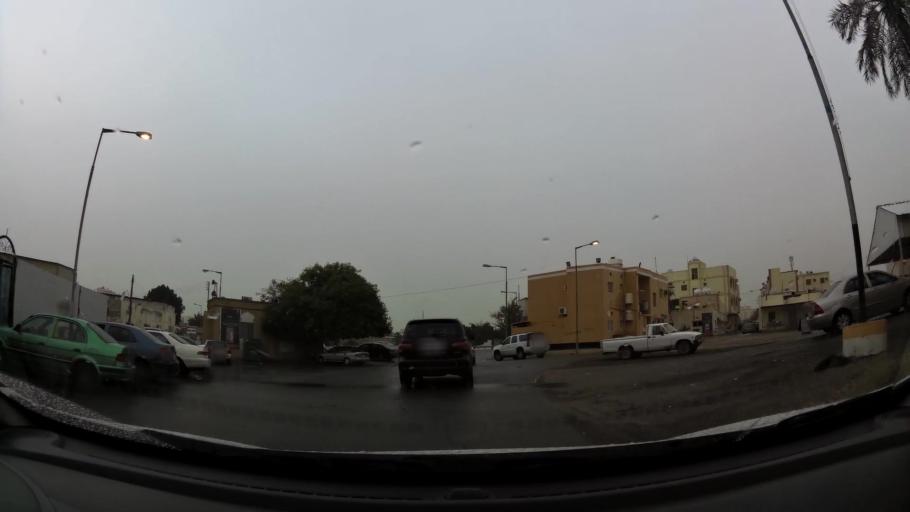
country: BH
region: Northern
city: Madinat `Isa
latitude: 26.1826
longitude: 50.5529
